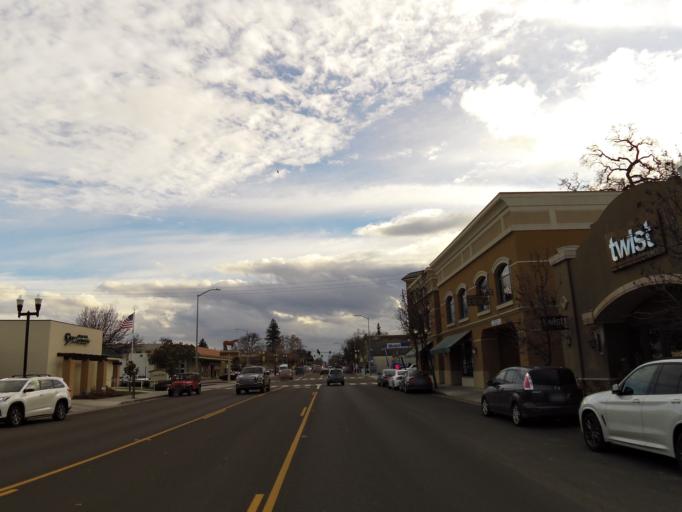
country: US
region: California
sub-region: San Luis Obispo County
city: Paso Robles
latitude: 35.6294
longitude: -120.6917
